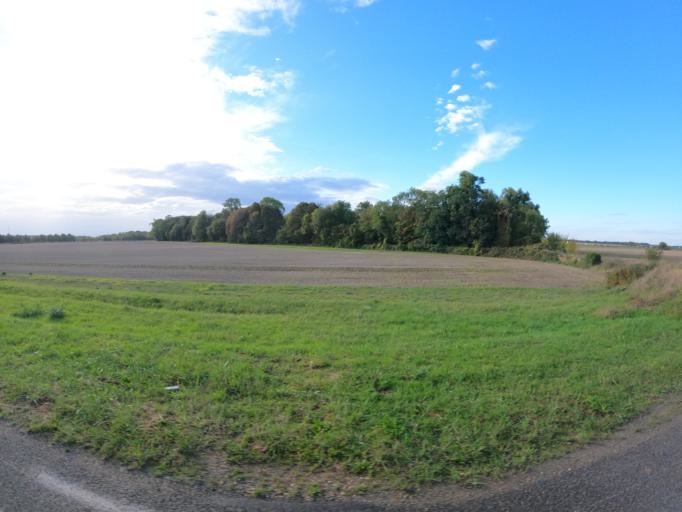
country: FR
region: Ile-de-France
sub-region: Departement de Seine-et-Marne
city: Serris
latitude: 48.8378
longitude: 2.7715
